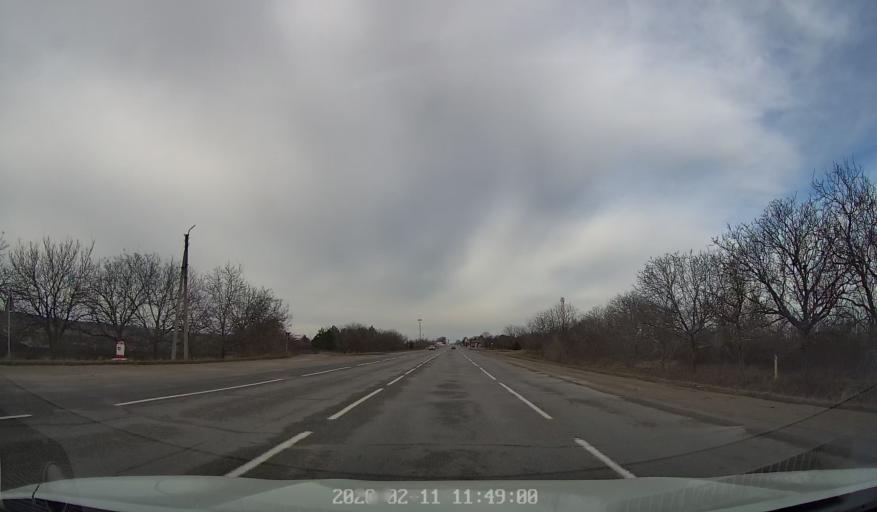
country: MD
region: Balti
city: Balti
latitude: 47.8449
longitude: 27.7959
